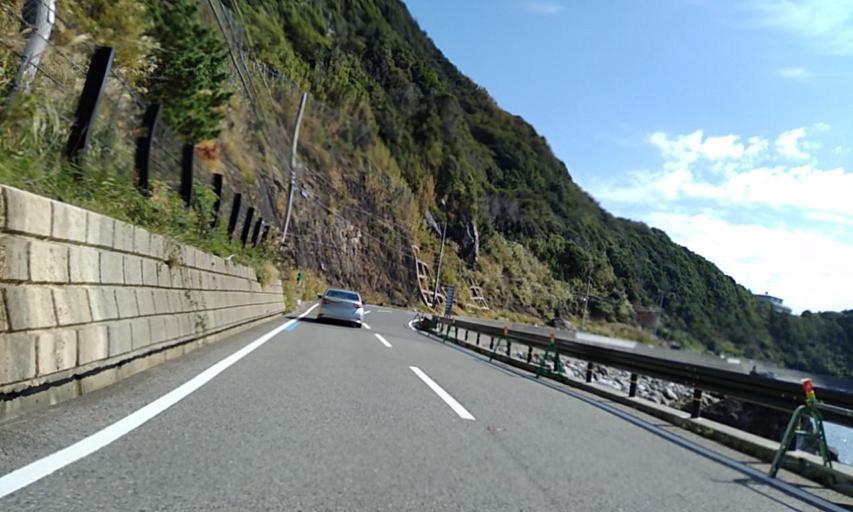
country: JP
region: Wakayama
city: Gobo
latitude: 33.9735
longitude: 135.0780
